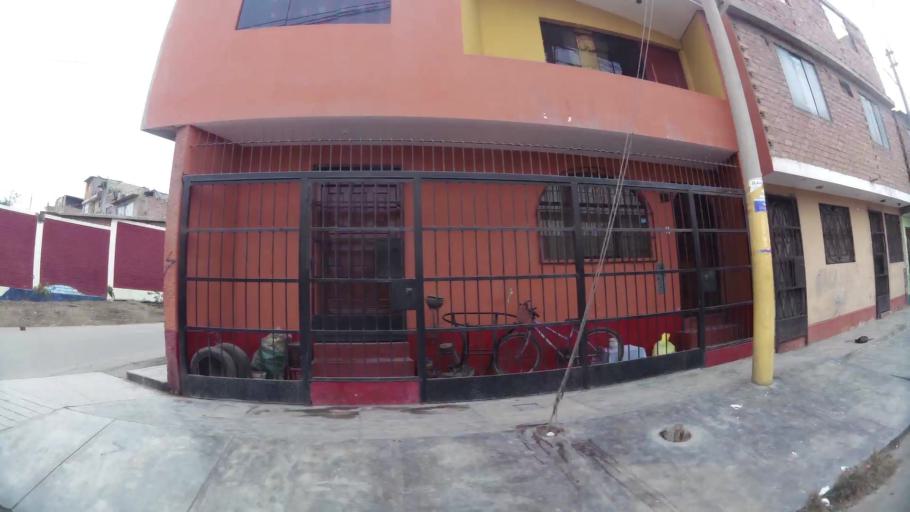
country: PE
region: Lima
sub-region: Lima
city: Surco
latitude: -12.1770
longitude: -76.9687
